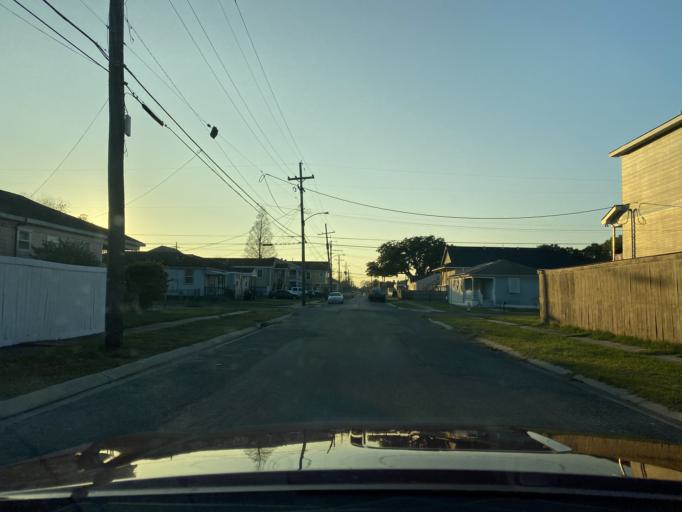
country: US
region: Louisiana
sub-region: Orleans Parish
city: New Orleans
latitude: 30.0216
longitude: -90.0502
